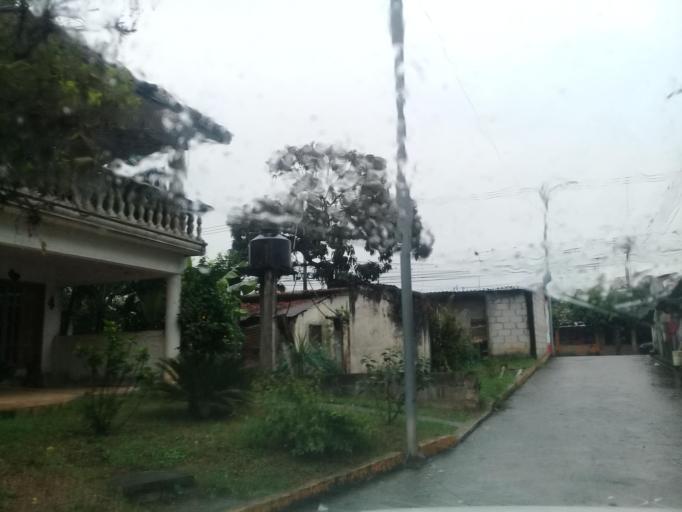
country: MX
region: Veracruz
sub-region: Cordoba
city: San Jose de Tapia
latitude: 18.8484
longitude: -96.9509
